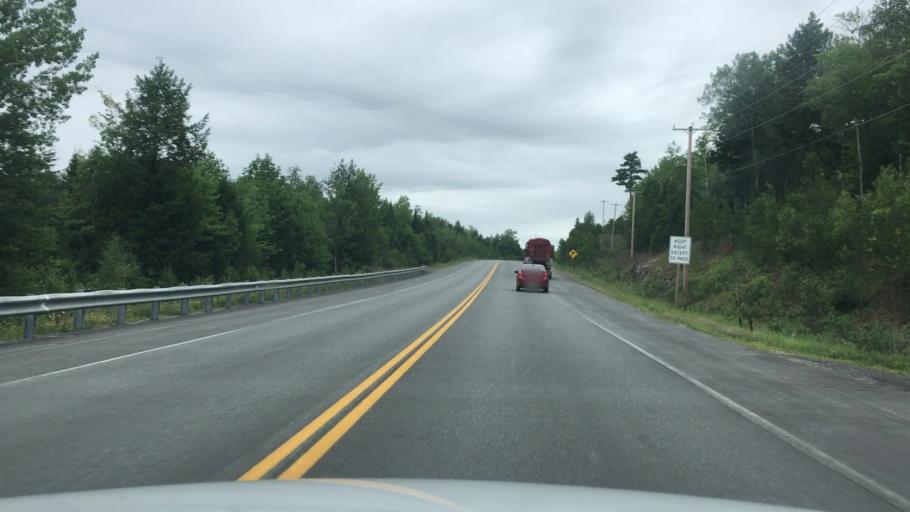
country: US
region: Maine
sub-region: Hancock County
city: Franklin
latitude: 44.8427
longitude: -68.3433
